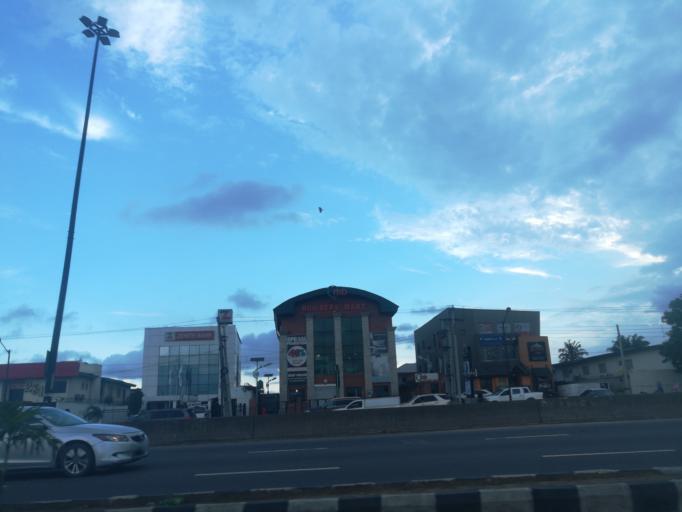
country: NG
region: Lagos
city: Somolu
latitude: 6.5498
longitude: 3.3779
